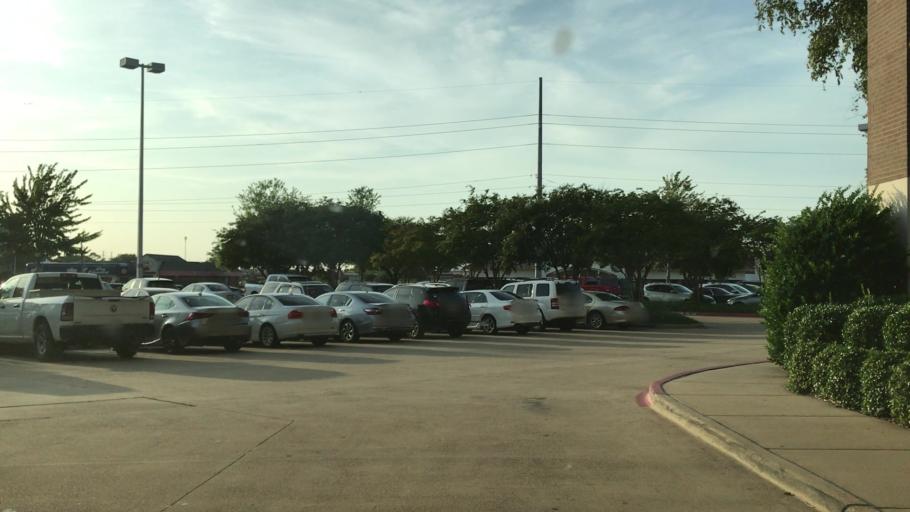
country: US
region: Louisiana
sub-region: Bossier Parish
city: Bossier City
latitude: 32.4315
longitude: -93.7099
